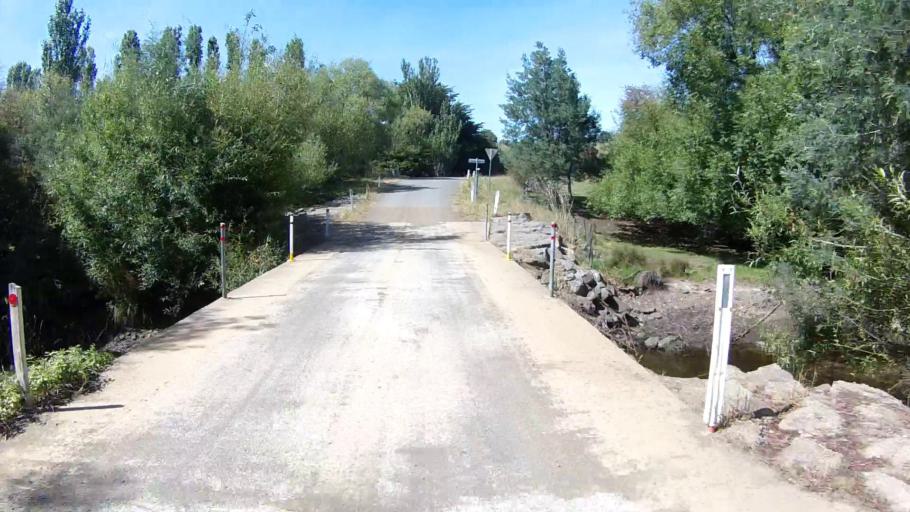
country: AU
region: Tasmania
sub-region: Sorell
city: Sorell
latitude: -42.7524
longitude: 147.6264
